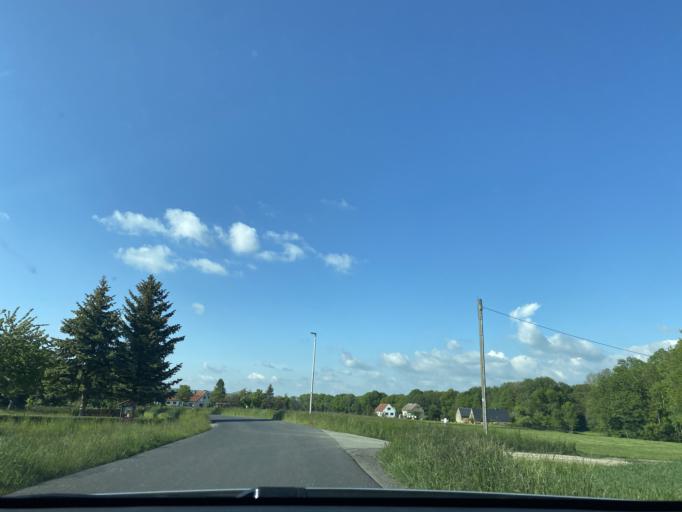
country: DE
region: Saxony
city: Reichenbach
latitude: 51.1099
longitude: 14.8325
